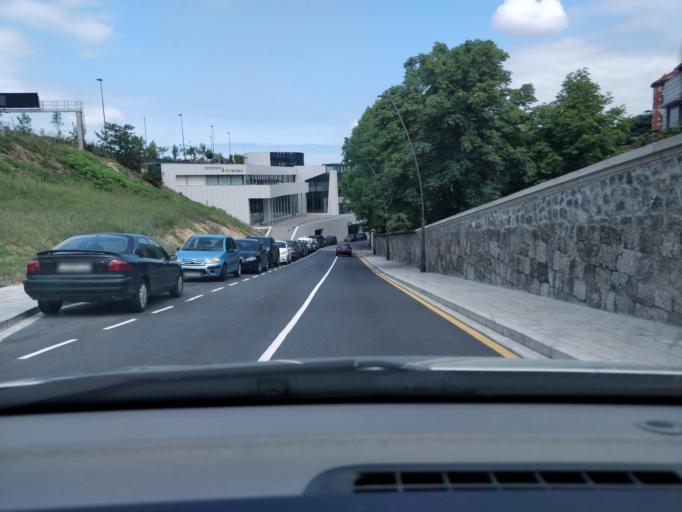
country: ES
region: Basque Country
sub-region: Bizkaia
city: Bilbao
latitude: 43.2613
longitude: -2.9548
